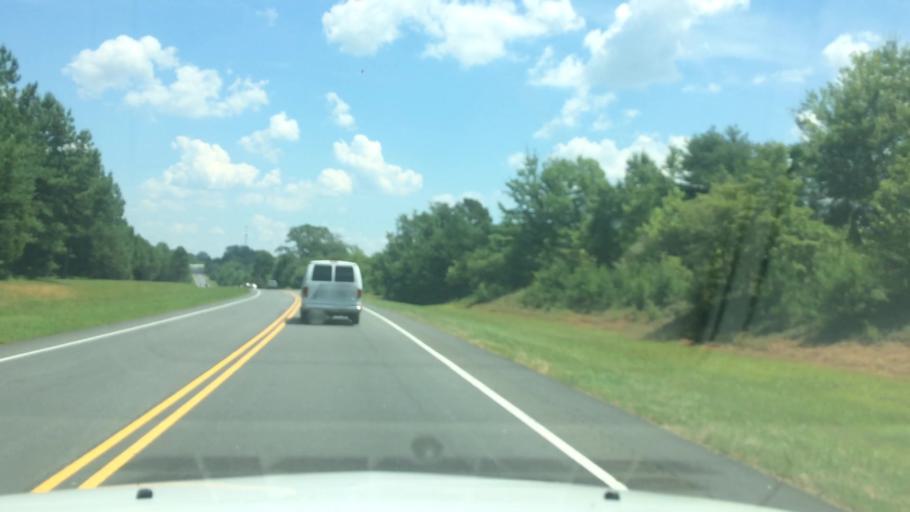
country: US
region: North Carolina
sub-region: Iredell County
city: Statesville
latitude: 35.8036
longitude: -80.9604
